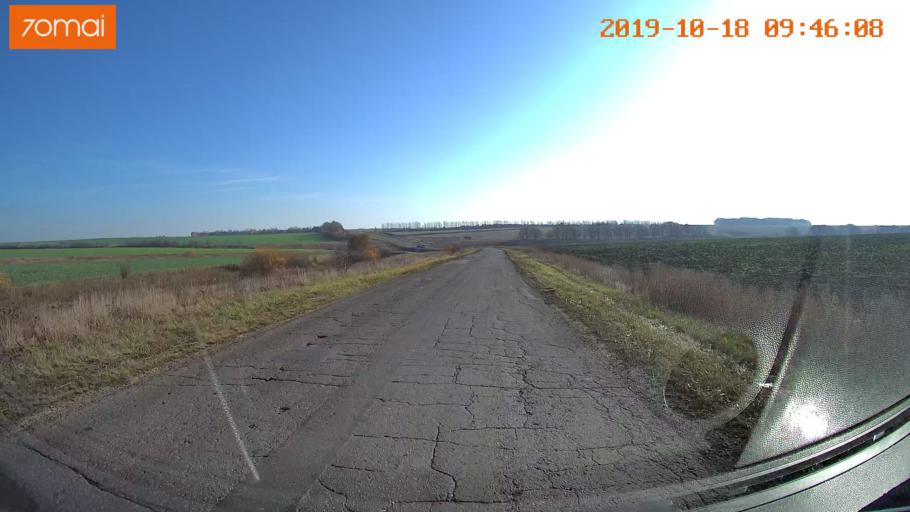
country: RU
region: Tula
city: Kazachka
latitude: 53.3123
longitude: 38.2069
